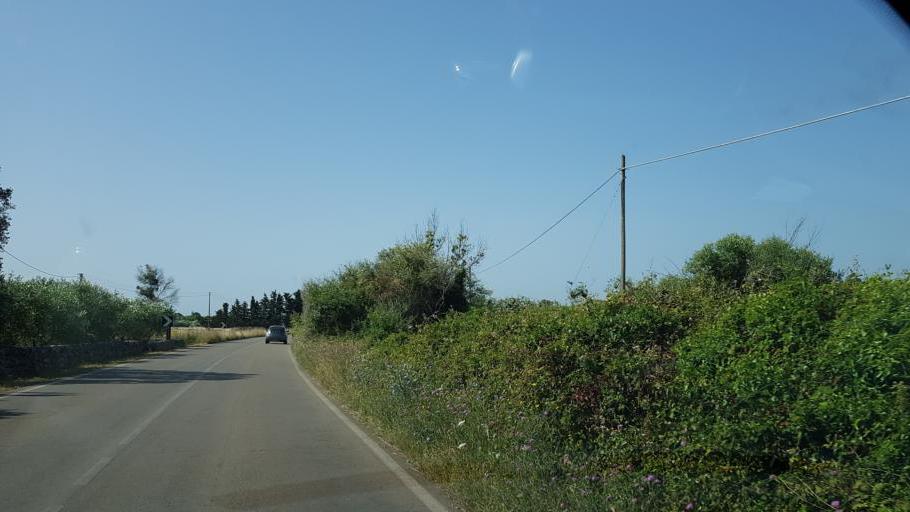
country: IT
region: Apulia
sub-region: Provincia di Lecce
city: Porto Cesareo
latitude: 40.3105
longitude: 17.8633
